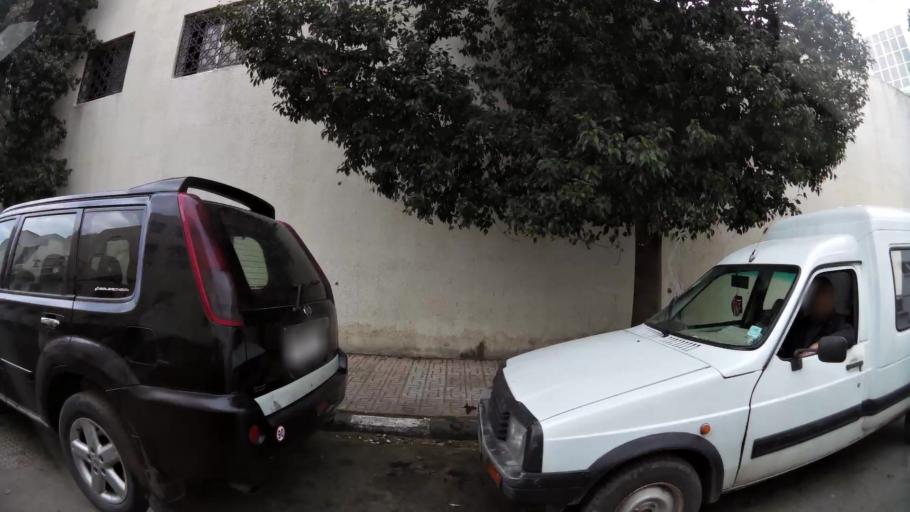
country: MA
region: Tanger-Tetouan
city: Tetouan
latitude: 35.5718
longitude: -5.3513
